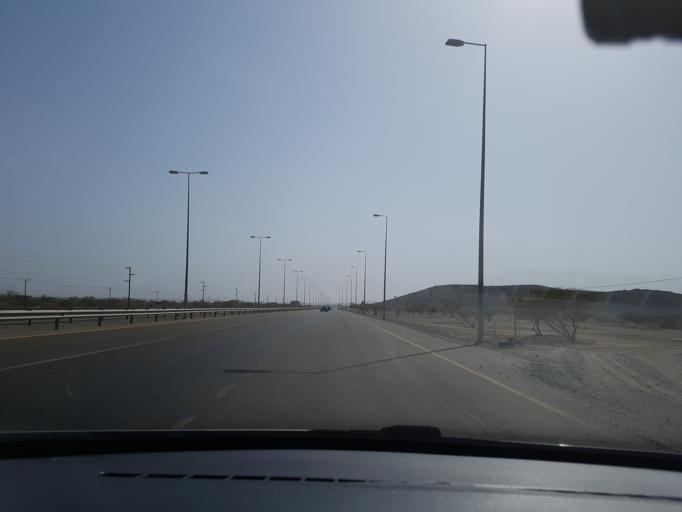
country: OM
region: Al Batinah
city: Al Liwa'
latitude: 24.4011
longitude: 56.5807
